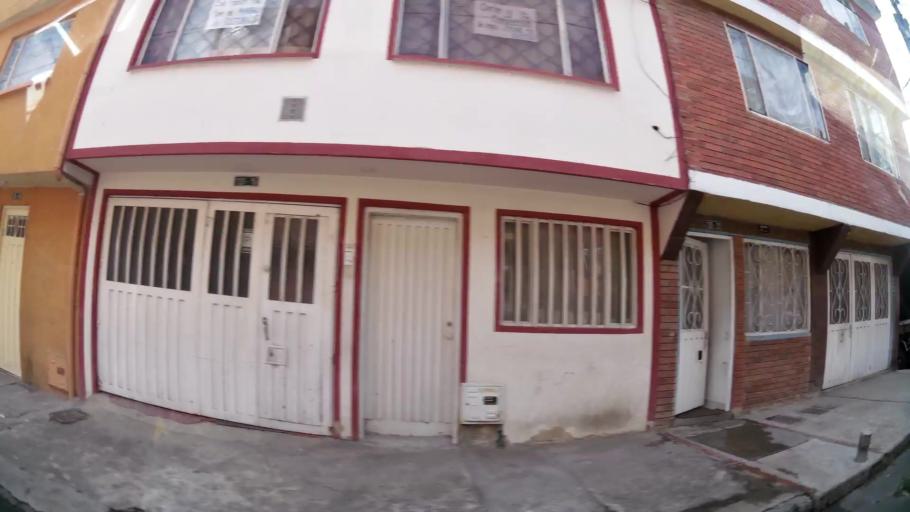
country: CO
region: Bogota D.C.
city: Barrio San Luis
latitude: 4.7191
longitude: -74.0878
